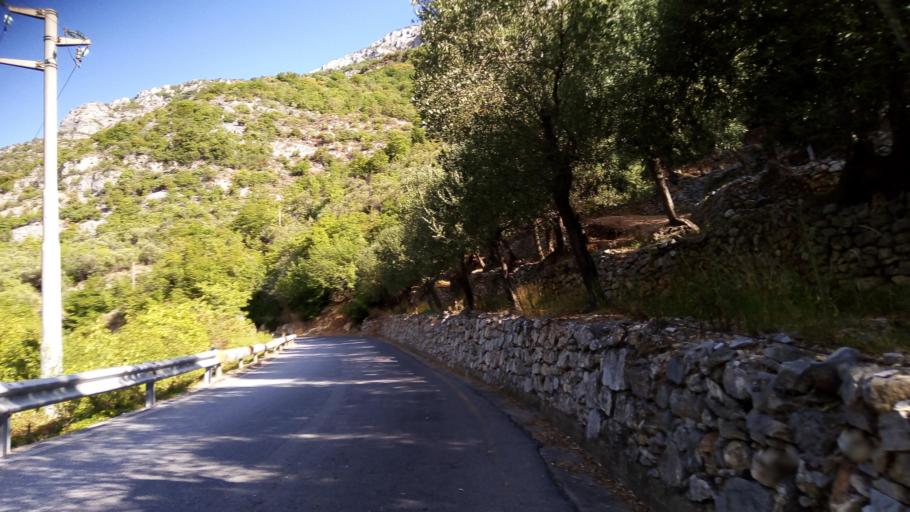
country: IT
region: Liguria
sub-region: Provincia di Savona
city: Toirano
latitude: 44.1369
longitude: 8.1972
